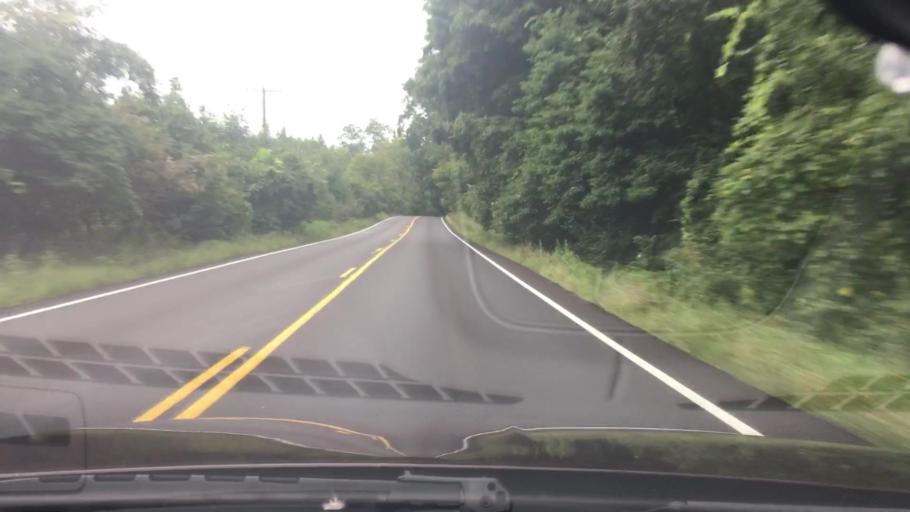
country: US
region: New York
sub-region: Dutchess County
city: Dover Plains
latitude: 41.8626
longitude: -73.5077
